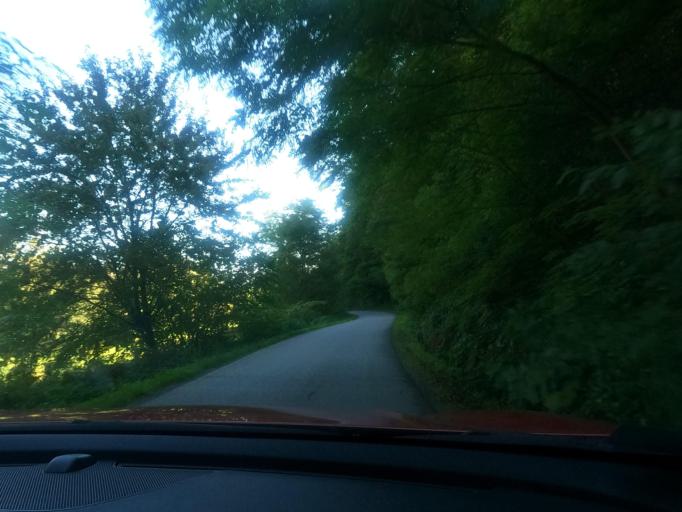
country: HR
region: Sisacko-Moslavacka
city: Petrinja
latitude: 45.4104
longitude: 16.2496
